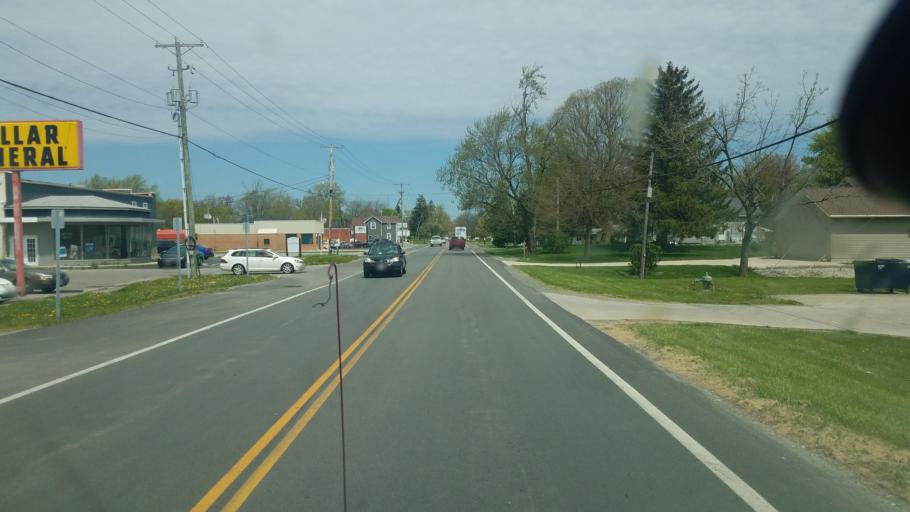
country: US
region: Ohio
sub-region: Hardin County
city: Ada
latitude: 40.7592
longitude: -83.8232
